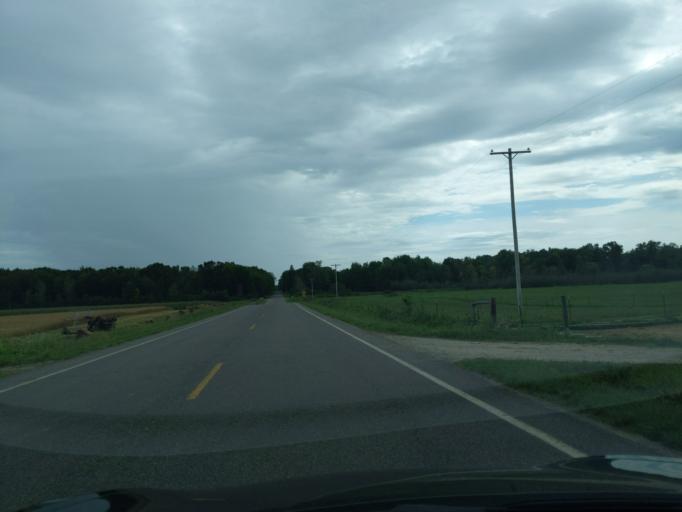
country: US
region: Michigan
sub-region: Clare County
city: Harrison
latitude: 44.0051
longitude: -84.9491
